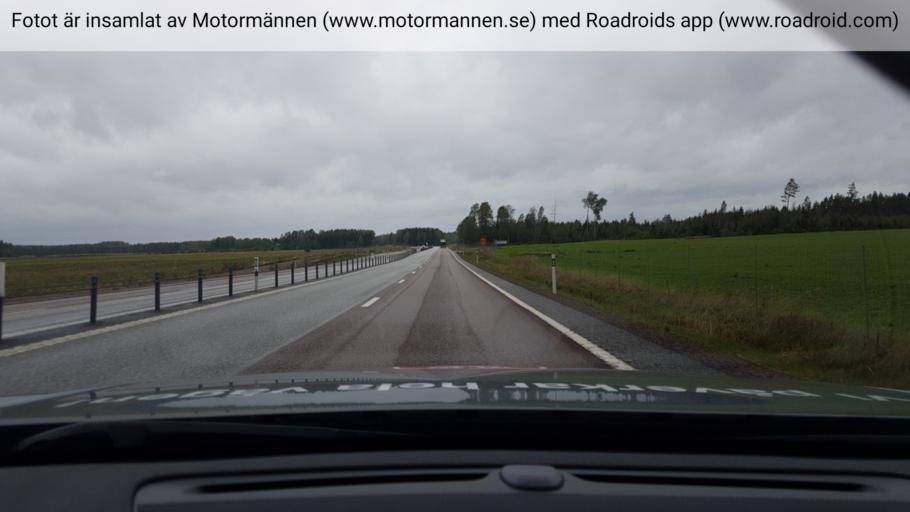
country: SE
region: Vaermland
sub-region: Kristinehamns Kommun
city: Kristinehamn
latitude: 59.3767
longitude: 13.9240
